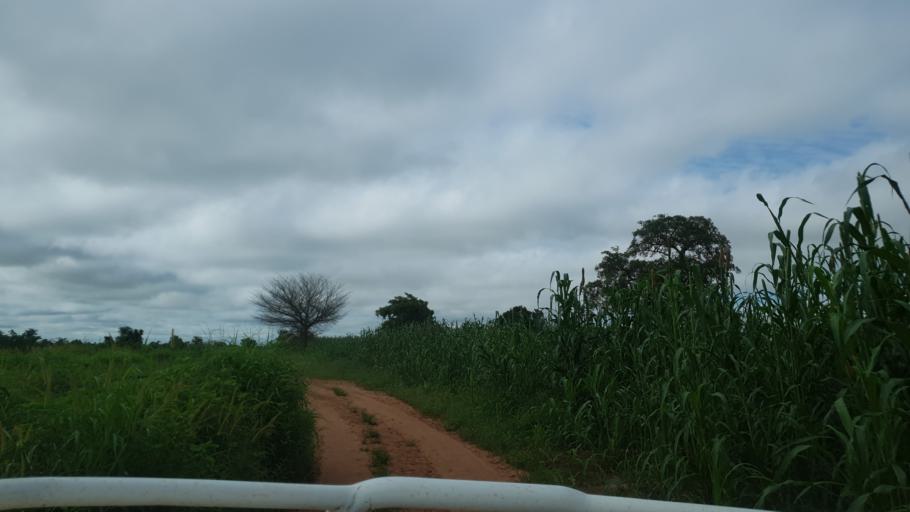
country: ML
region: Segou
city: Baroueli
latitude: 13.4987
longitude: -6.8972
